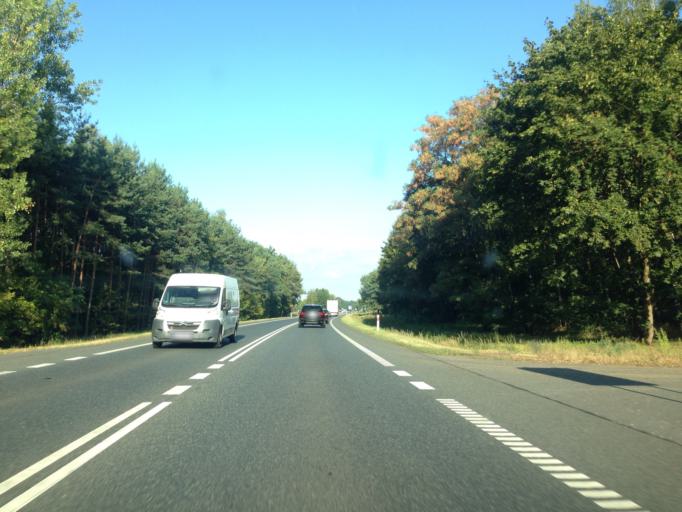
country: PL
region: Kujawsko-Pomorskie
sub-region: Powiat bydgoski
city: Solec Kujawski
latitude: 53.0616
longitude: 18.1810
